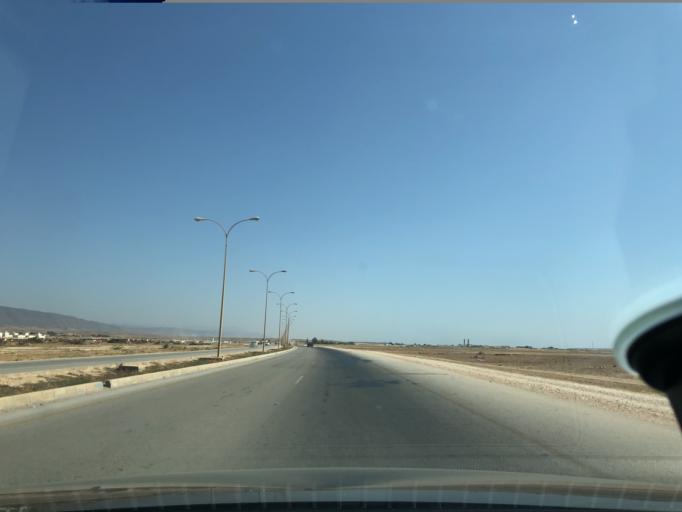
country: OM
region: Zufar
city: Salalah
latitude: 17.0530
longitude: 54.2814
